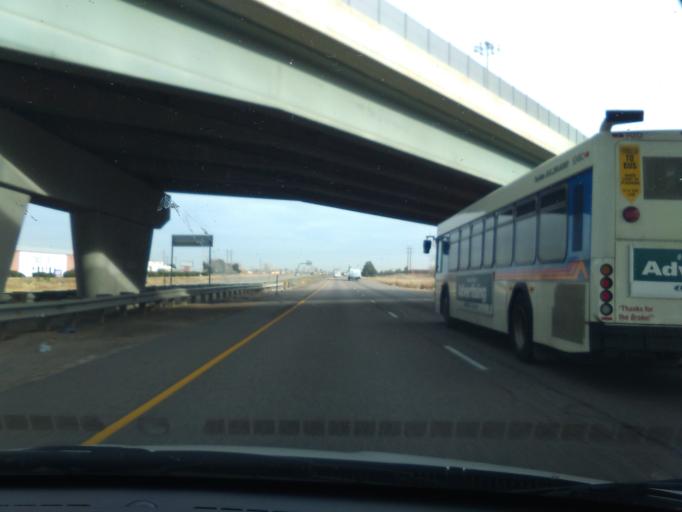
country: US
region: Colorado
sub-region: Adams County
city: Derby
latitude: 39.8851
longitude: -104.8687
